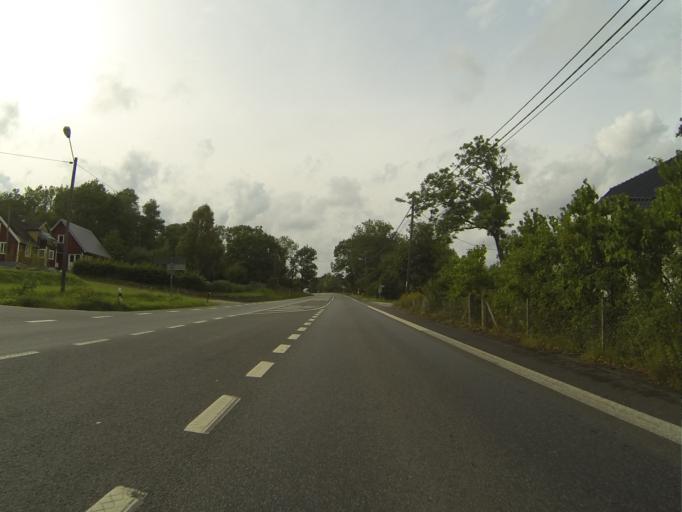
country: SE
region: Skane
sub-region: Kristianstads Kommun
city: Onnestad
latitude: 55.9411
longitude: 13.9043
